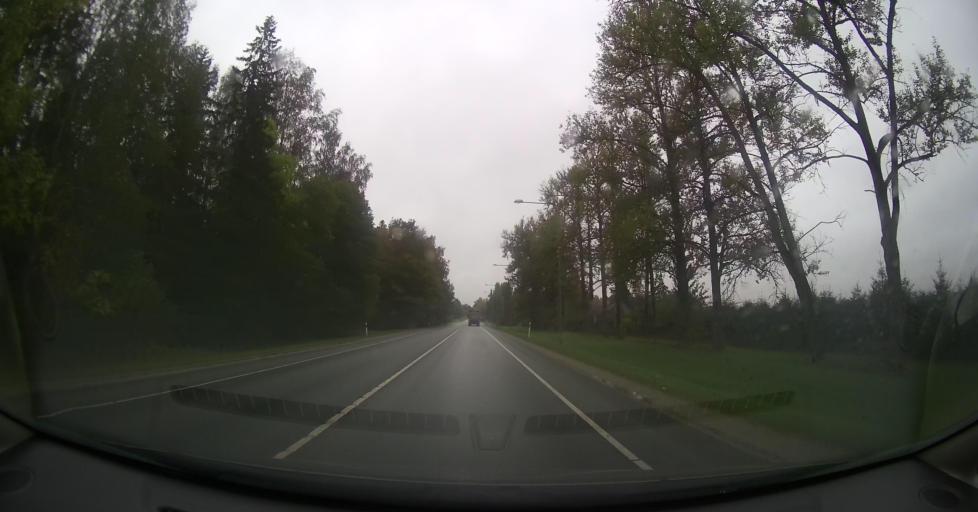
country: EE
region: Jaervamaa
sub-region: Paide linn
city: Paide
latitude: 59.0085
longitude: 25.5952
